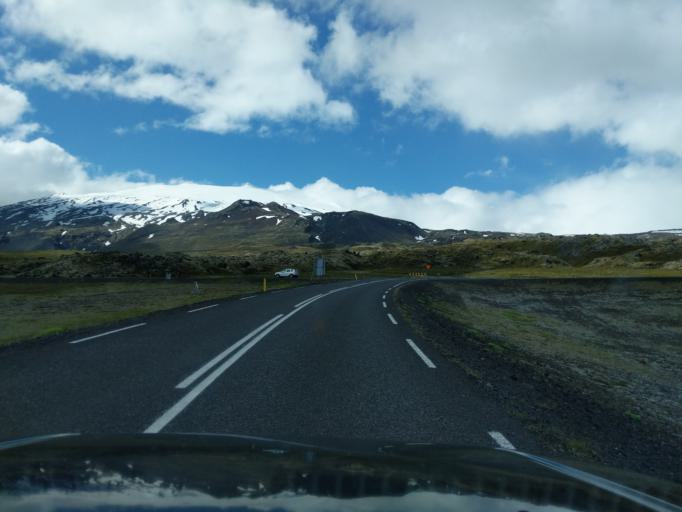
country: IS
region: West
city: Olafsvik
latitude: 64.7615
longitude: -23.6765
